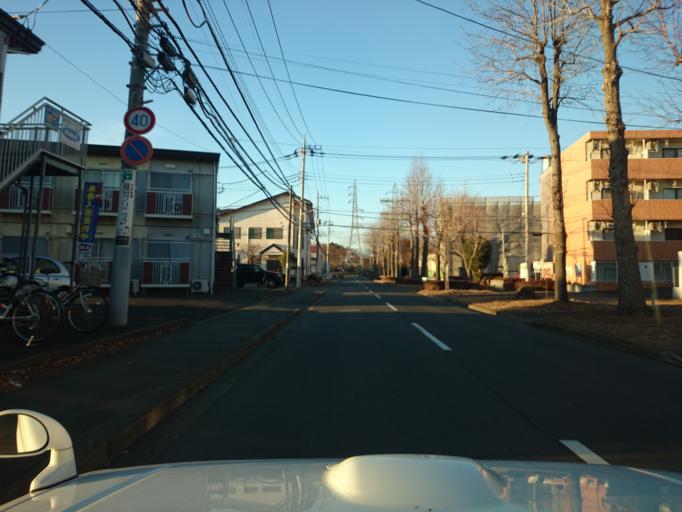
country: JP
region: Ibaraki
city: Naka
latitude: 36.1044
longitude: 140.0991
